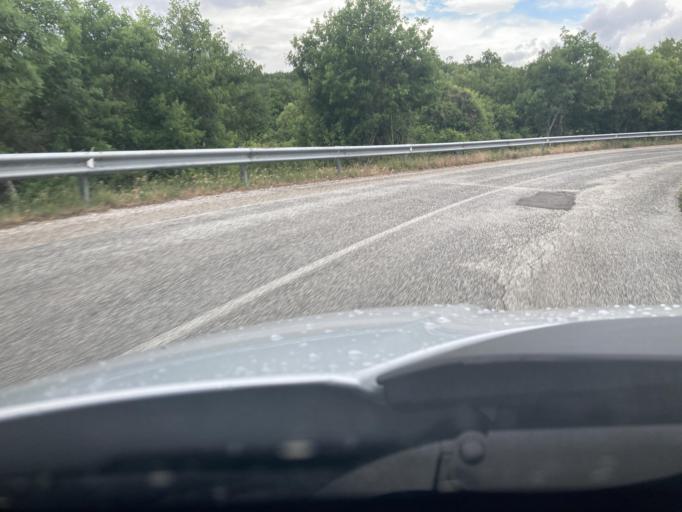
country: IT
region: Abruzzo
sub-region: Provincia dell' Aquila
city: San Panfilo d'Ocre
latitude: 42.2748
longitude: 13.4771
